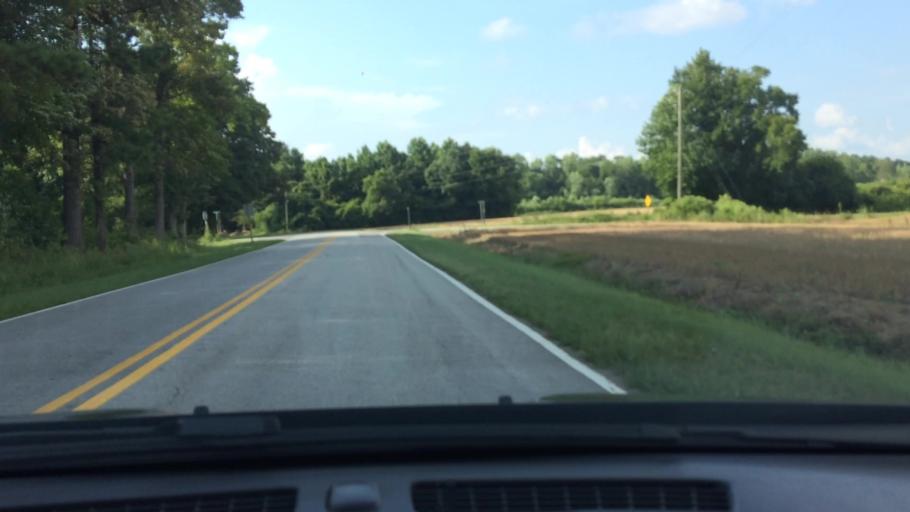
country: US
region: North Carolina
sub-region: Beaufort County
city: River Road
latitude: 35.4569
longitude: -77.0207
